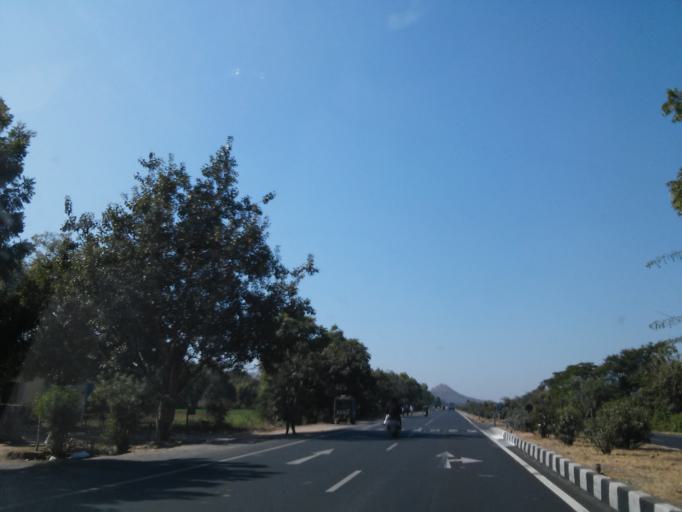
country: IN
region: Gujarat
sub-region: Sabar Kantha
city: Modasa
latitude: 23.6203
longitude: 73.2826
